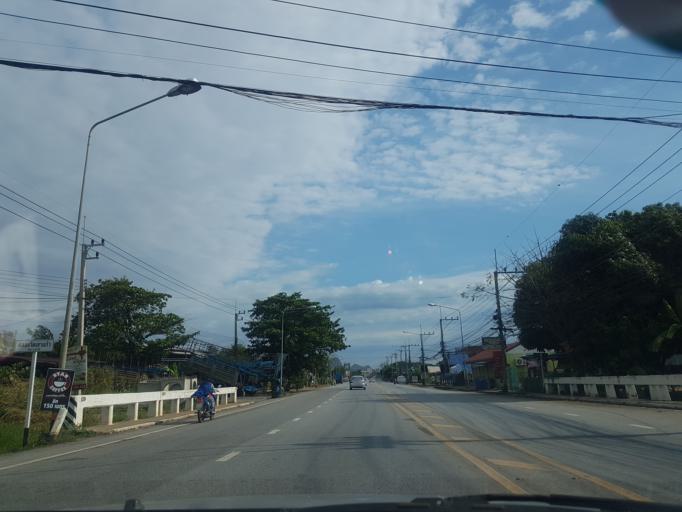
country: TH
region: Lop Buri
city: Lop Buri
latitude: 14.7864
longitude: 100.6982
